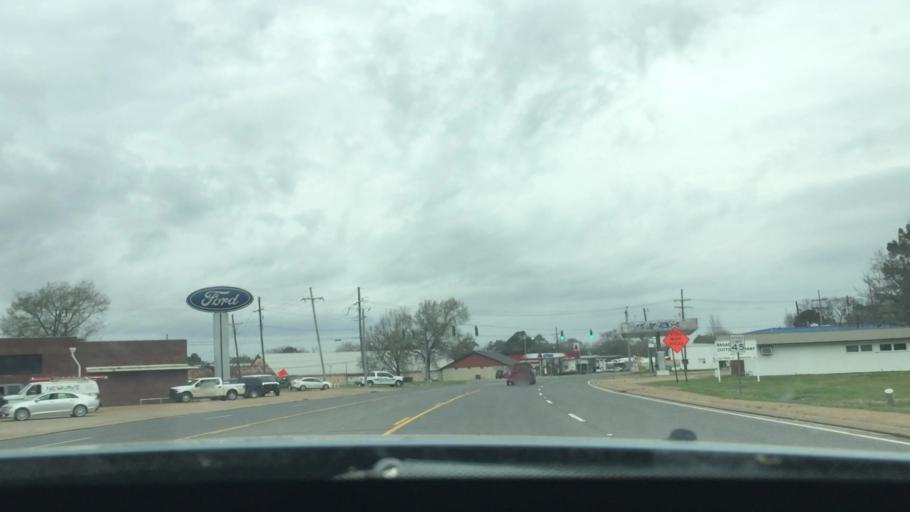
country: US
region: Louisiana
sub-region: Franklin Parish
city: Winnsboro
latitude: 32.1555
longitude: -91.7134
